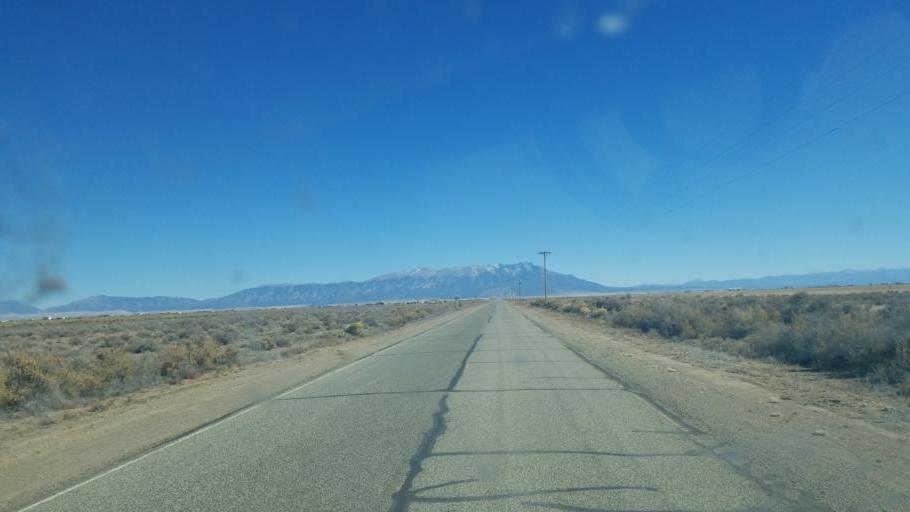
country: US
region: Colorado
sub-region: Alamosa County
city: Alamosa
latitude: 37.5744
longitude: -105.9282
